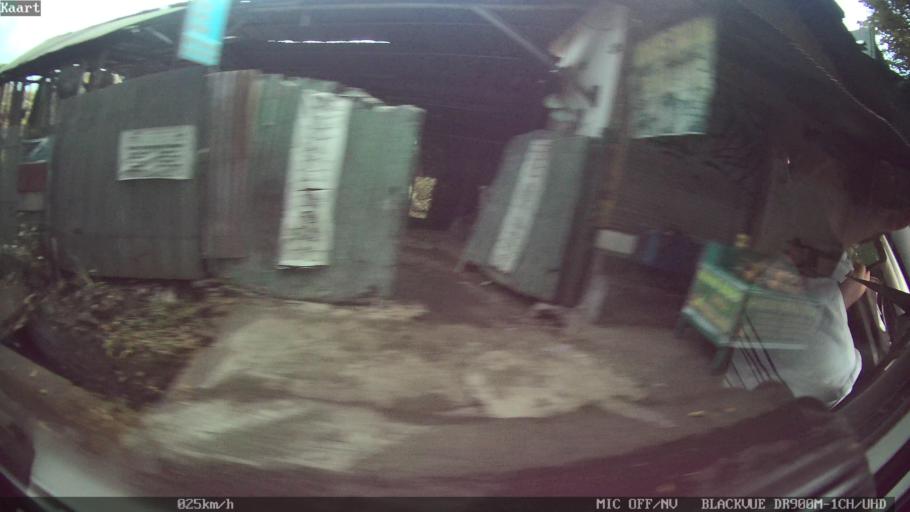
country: ID
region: Bali
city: Banjar Karangsuling
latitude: -8.6058
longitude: 115.1900
